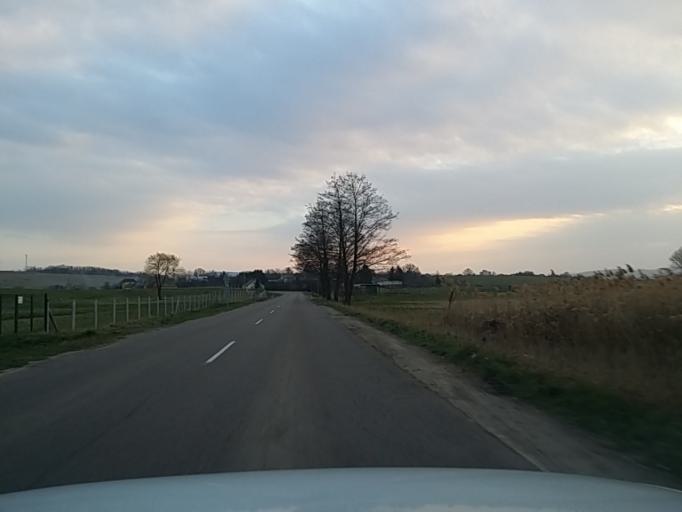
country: HU
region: Nograd
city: Batonyterenye
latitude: 47.9991
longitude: 19.8500
